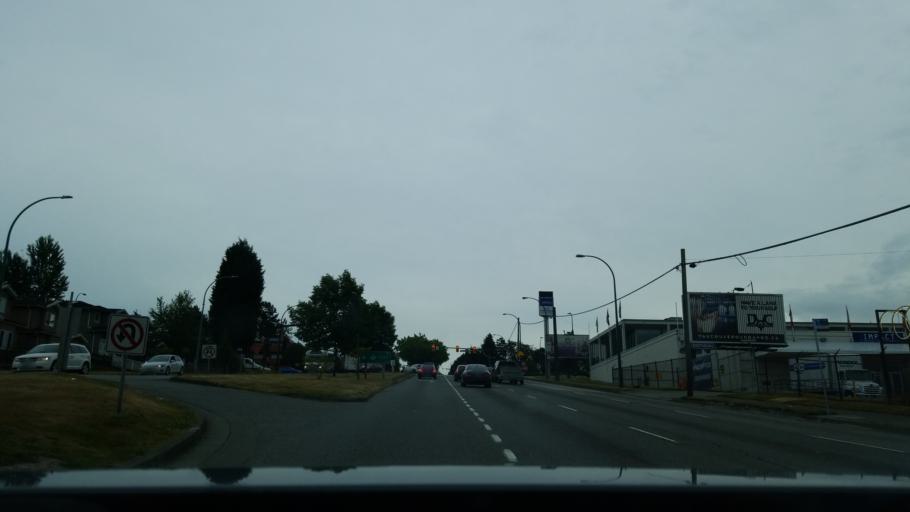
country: CA
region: British Columbia
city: Burnaby
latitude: 49.2593
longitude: -123.0237
